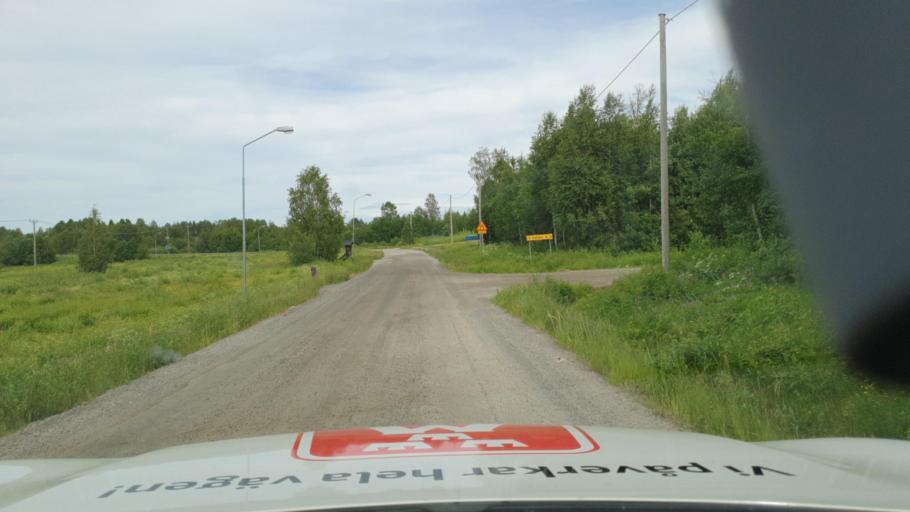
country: SE
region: Vaesterbotten
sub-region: Skelleftea Kommun
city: Viken
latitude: 64.5145
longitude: 20.9491
